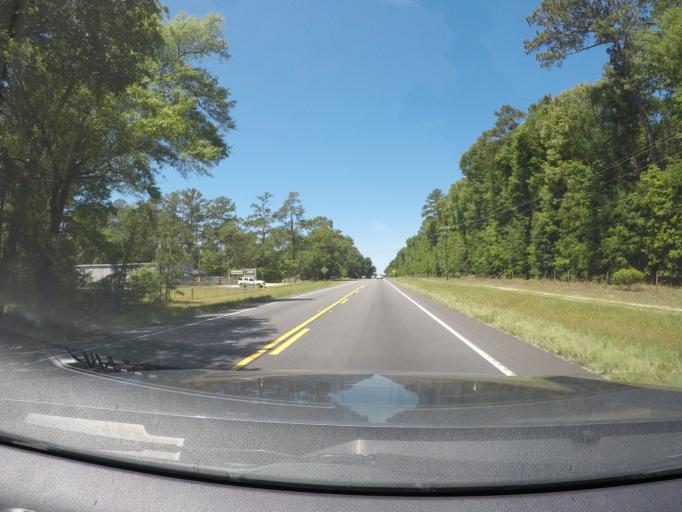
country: US
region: Georgia
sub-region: Chatham County
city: Bloomingdale
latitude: 32.1929
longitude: -81.4240
